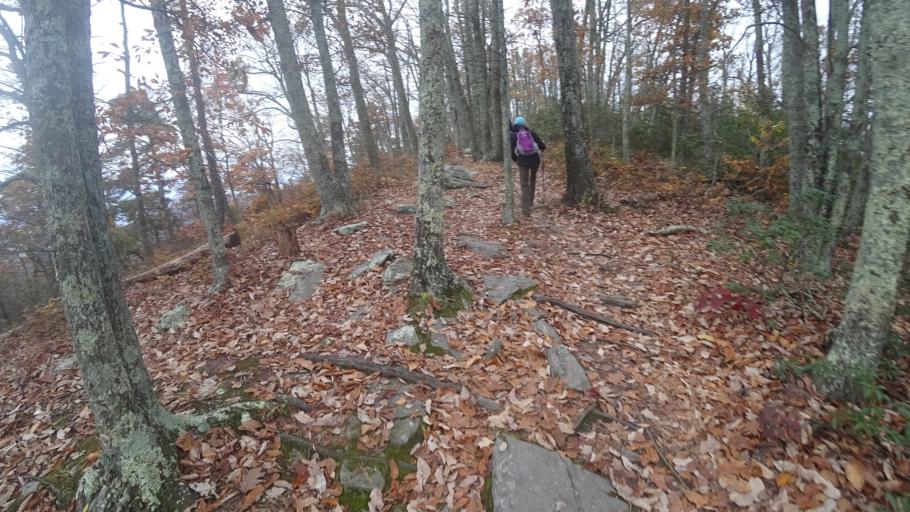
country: US
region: Virginia
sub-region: Rockingham County
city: Massanutten
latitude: 38.4185
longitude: -78.7534
